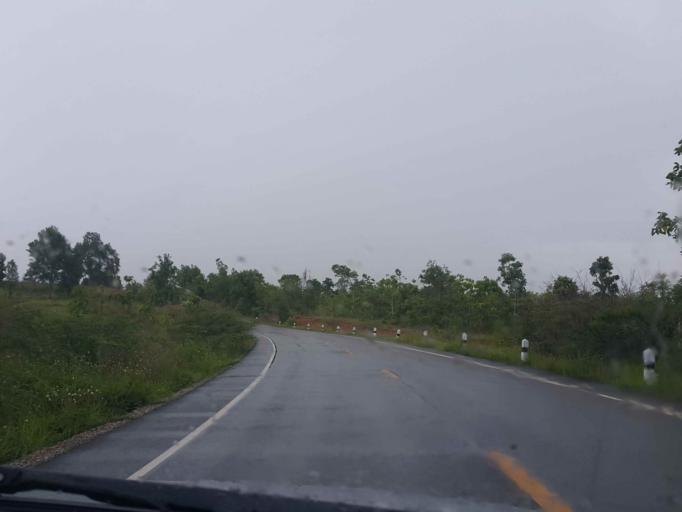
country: TH
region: Phayao
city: Dok Kham Tai
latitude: 19.0291
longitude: 99.9661
